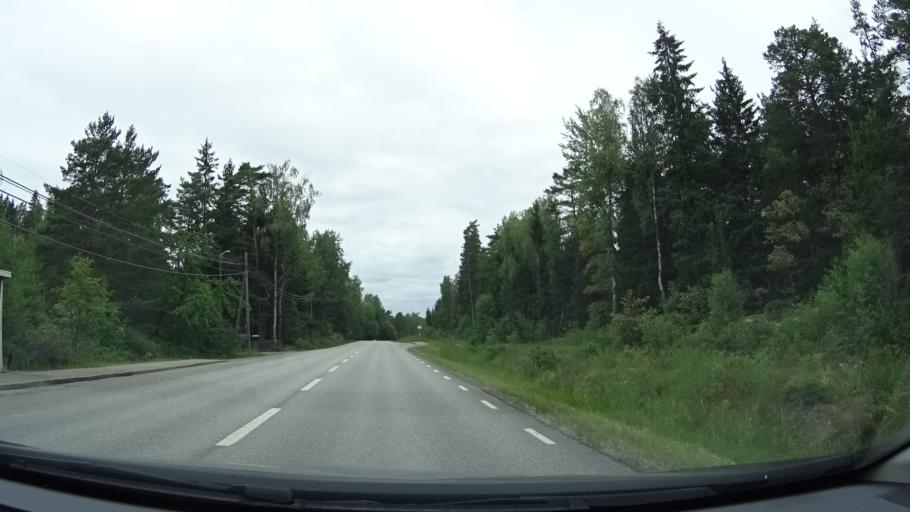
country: SE
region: Stockholm
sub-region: Varmdo Kommun
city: Hemmesta
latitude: 59.3432
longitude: 18.4810
